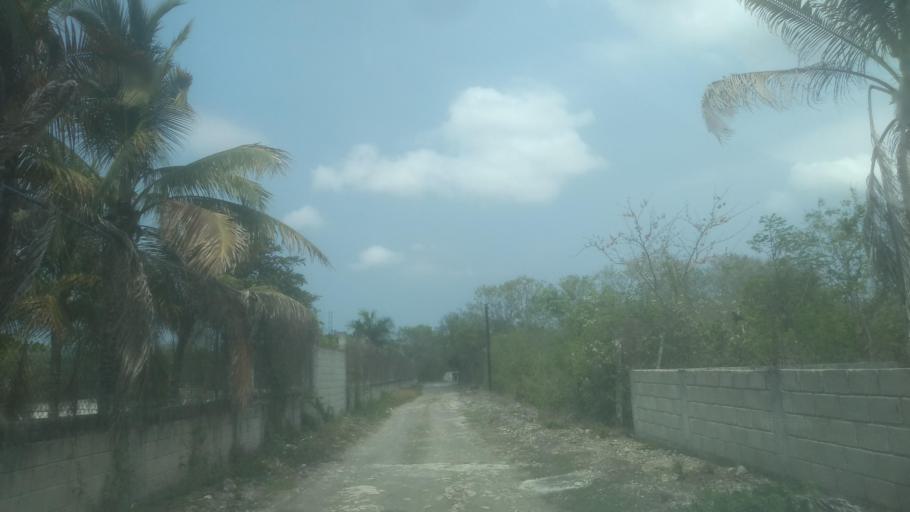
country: MX
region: Veracruz
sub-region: Emiliano Zapata
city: Plan del Rio
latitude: 19.3901
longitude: -96.6319
